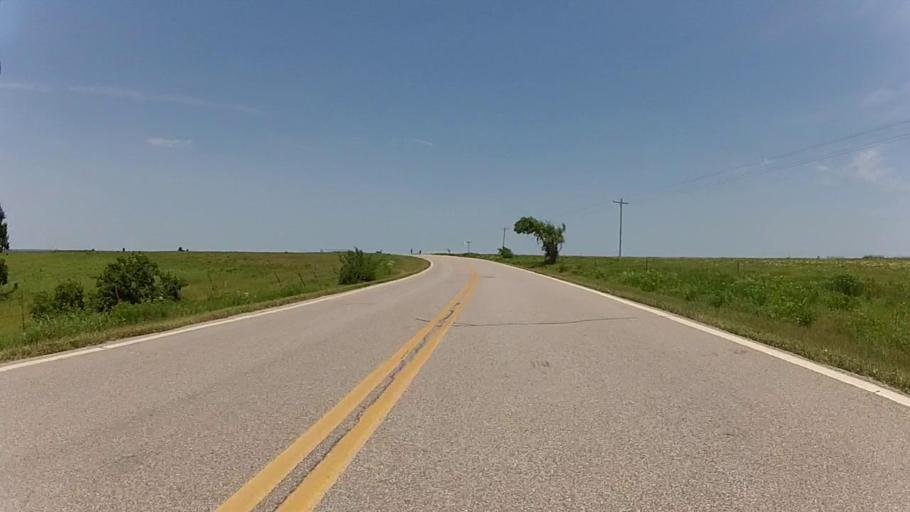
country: US
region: Kansas
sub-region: Chautauqua County
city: Sedan
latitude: 37.1112
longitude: -96.2441
